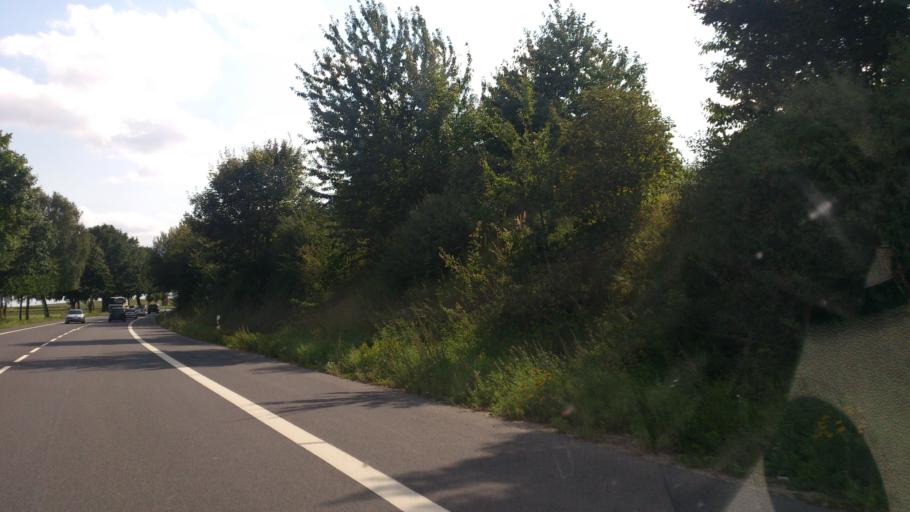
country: DE
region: North Rhine-Westphalia
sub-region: Regierungsbezirk Koln
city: Erftstadt
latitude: 50.7700
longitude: 6.7319
